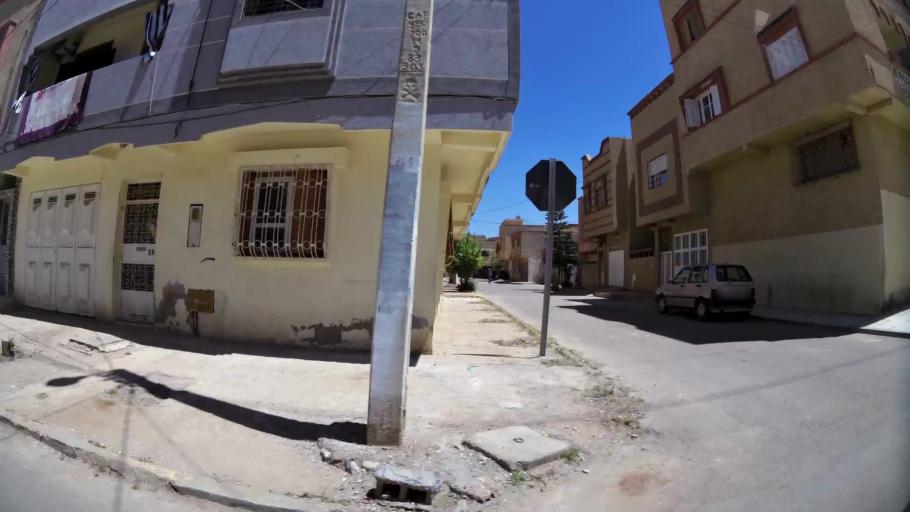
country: MA
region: Oriental
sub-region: Oujda-Angad
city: Oujda
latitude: 34.6583
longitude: -1.9255
